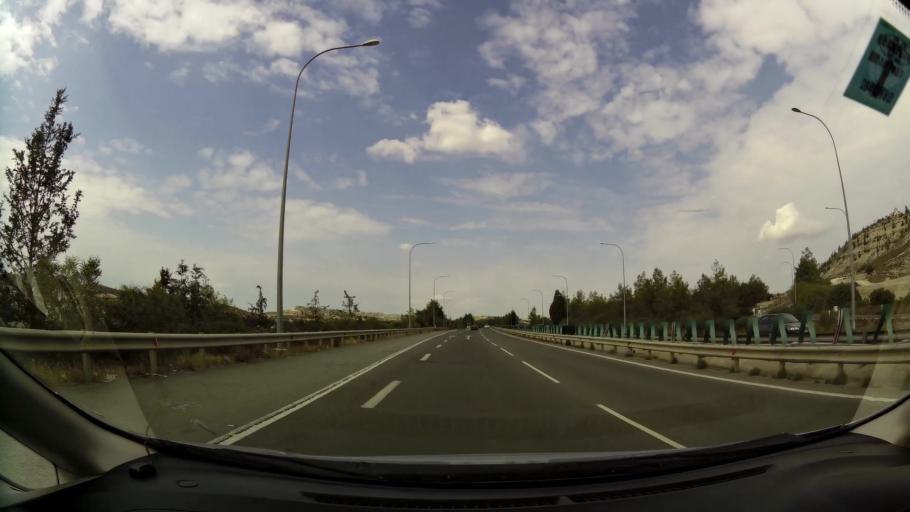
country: CY
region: Lefkosia
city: Alampra
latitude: 35.0015
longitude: 33.3984
